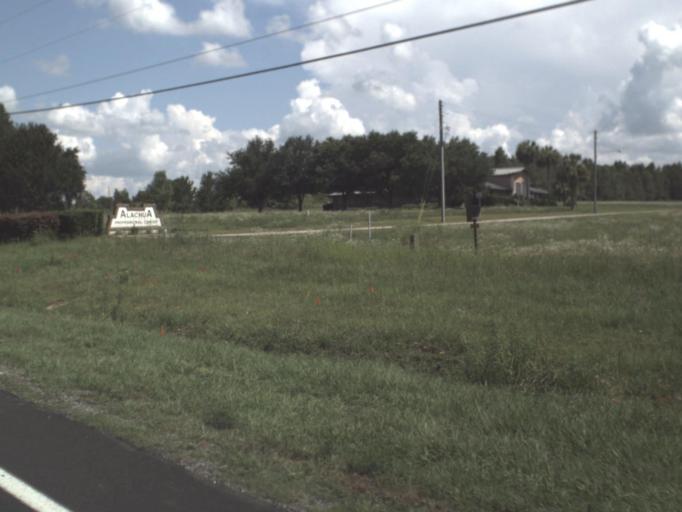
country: US
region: Florida
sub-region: Alachua County
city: Alachua
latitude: 29.7817
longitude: -82.4576
